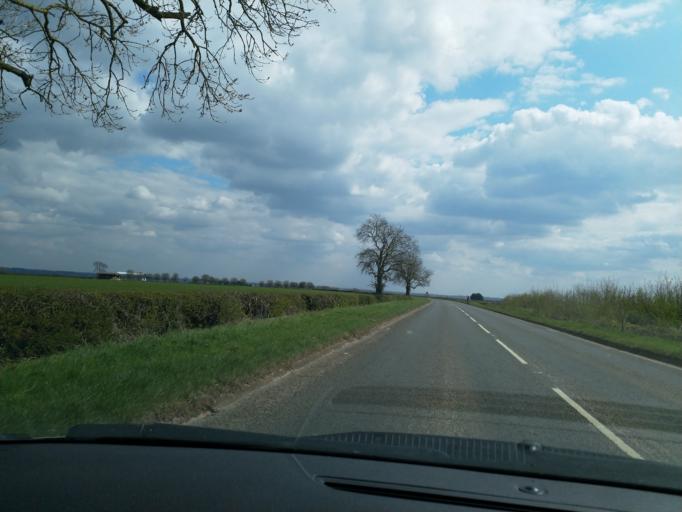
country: GB
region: England
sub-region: Oxfordshire
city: Hanwell
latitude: 52.1148
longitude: -1.3993
